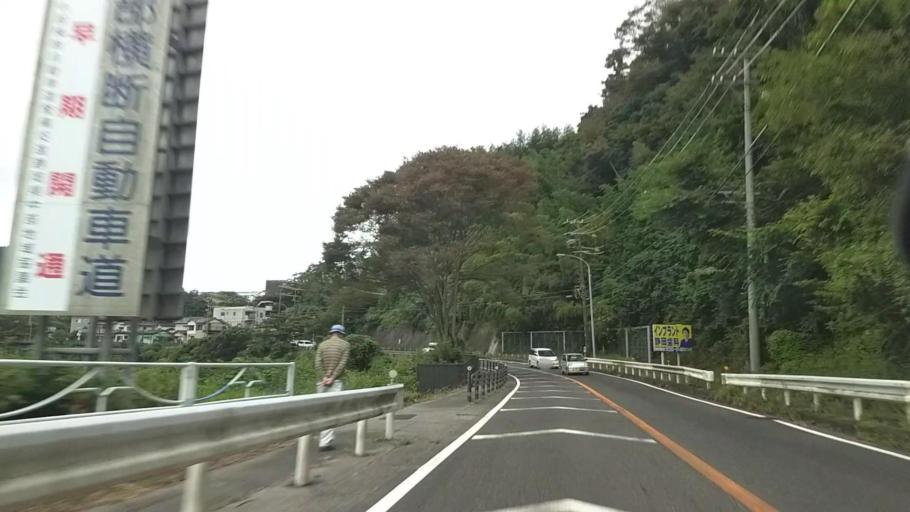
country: JP
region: Shizuoka
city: Fujinomiya
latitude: 35.0947
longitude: 138.5135
